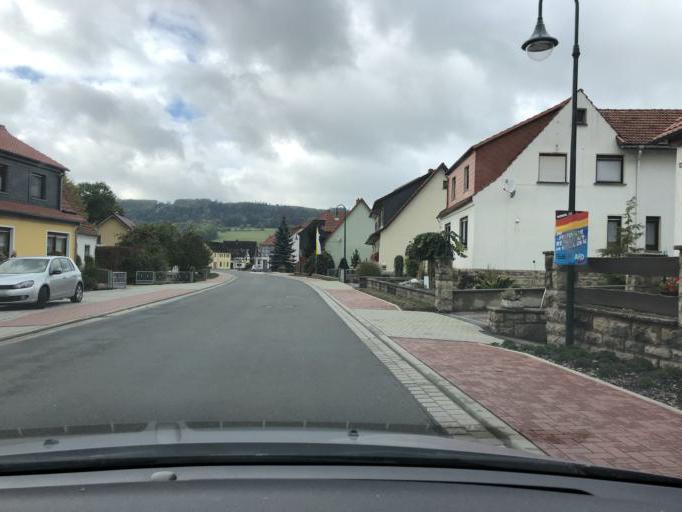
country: DE
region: Thuringia
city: Grossbartloff
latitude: 51.2510
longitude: 10.2177
